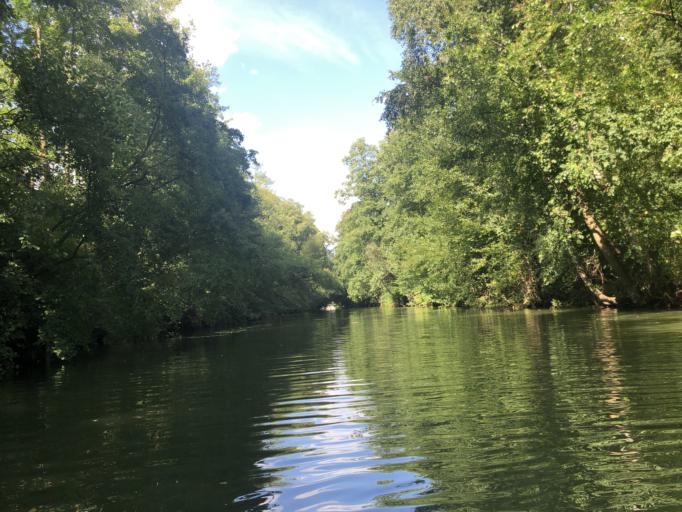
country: DE
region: Brandenburg
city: Mullrose
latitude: 52.2407
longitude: 14.4271
